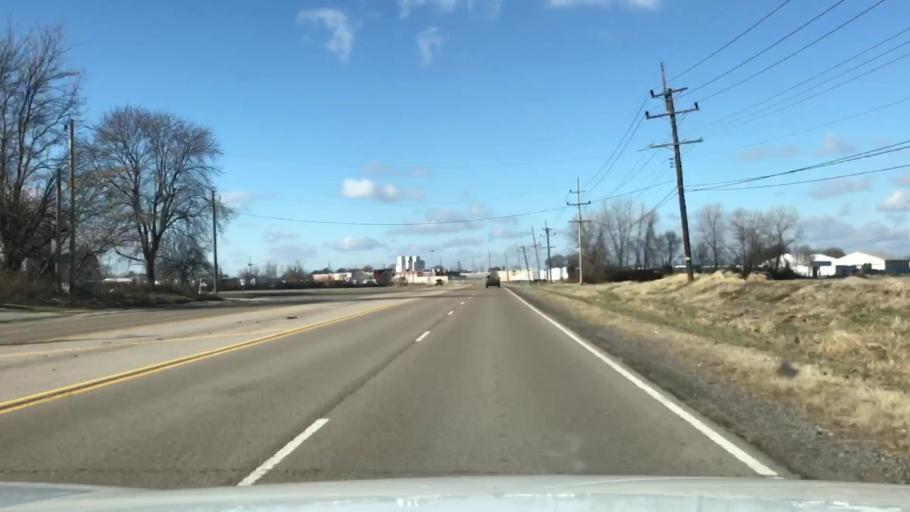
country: US
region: Illinois
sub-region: Saint Clair County
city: Washington Park
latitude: 38.6126
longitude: -90.0856
